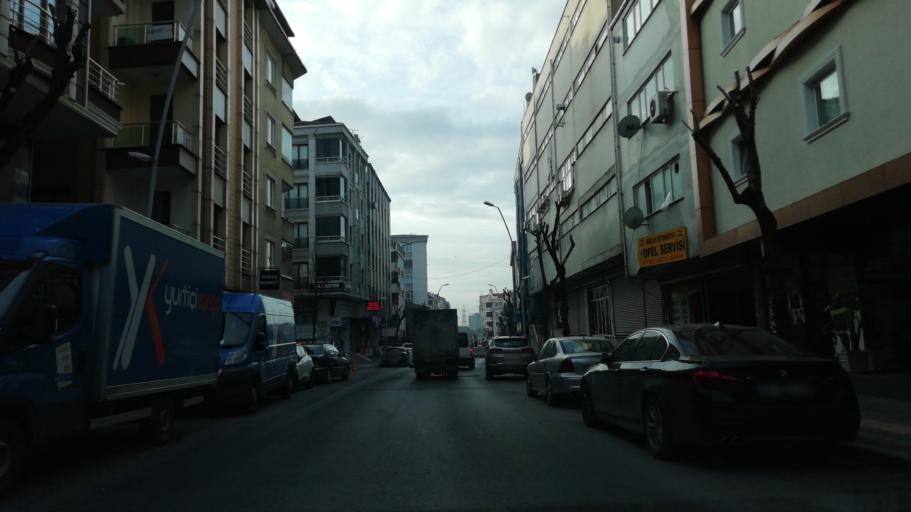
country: TR
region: Istanbul
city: Bahcelievler
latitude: 41.0021
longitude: 28.8268
